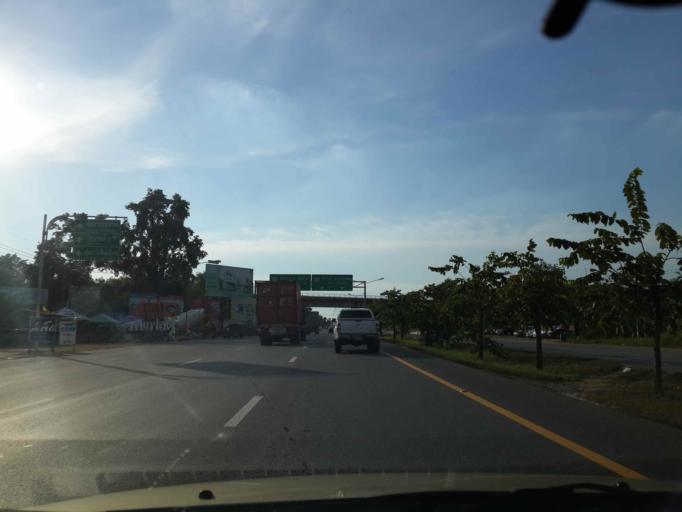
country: TH
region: Chon Buri
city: Bang Lamung
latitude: 12.9972
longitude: 100.9348
